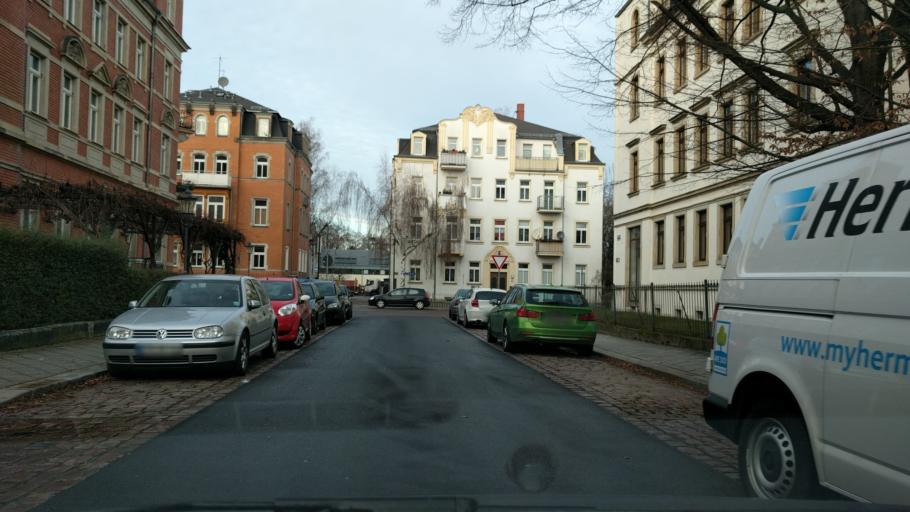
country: DE
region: Saxony
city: Dresden
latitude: 51.0376
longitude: 13.6983
